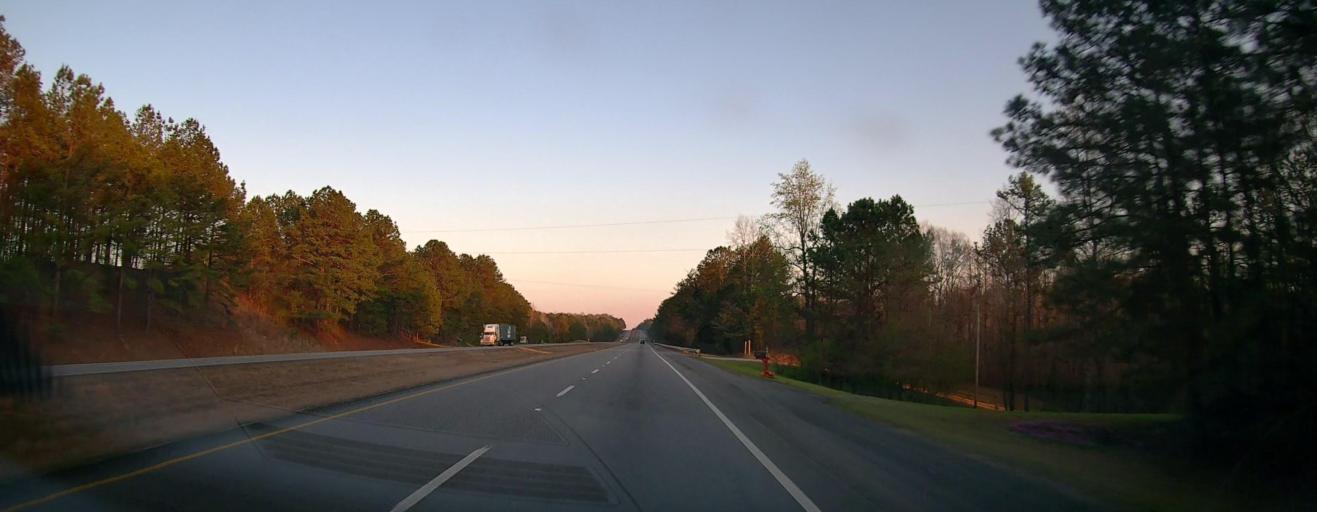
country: US
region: Alabama
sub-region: Coosa County
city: Goodwater
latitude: 33.0314
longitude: -86.1157
